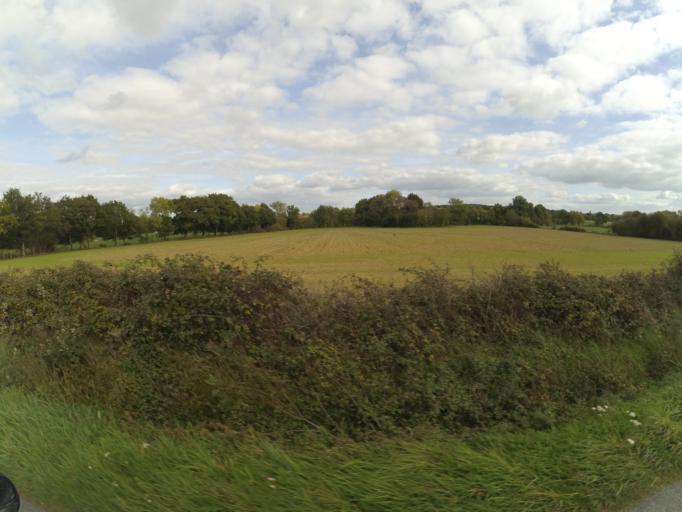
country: FR
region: Pays de la Loire
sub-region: Departement de la Loire-Atlantique
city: Bouvron
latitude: 47.4671
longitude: -1.8359
